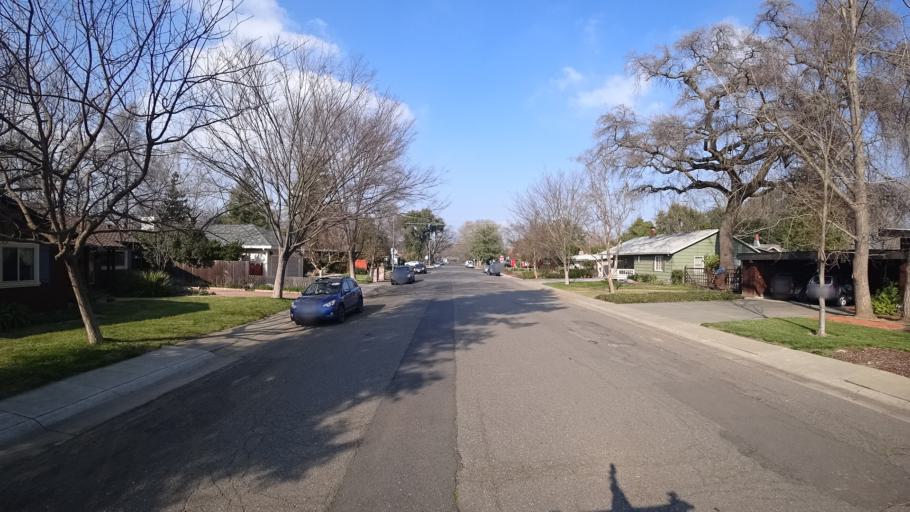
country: US
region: California
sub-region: Yolo County
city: Davis
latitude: 38.5500
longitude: -121.7490
